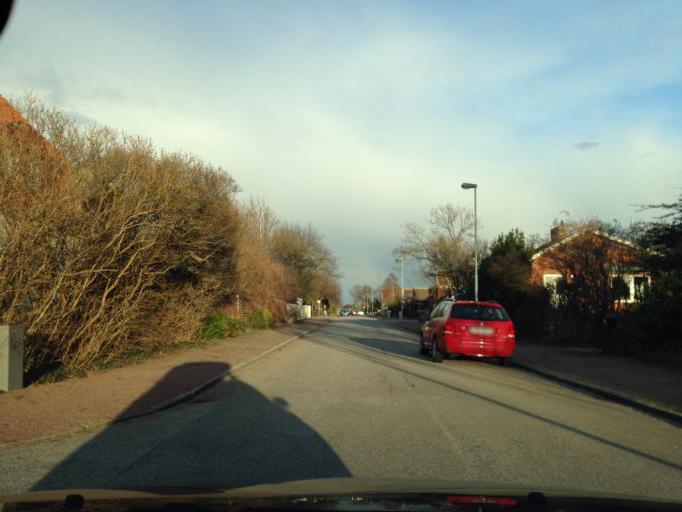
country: SE
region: Skane
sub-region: Malmo
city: Bunkeflostrand
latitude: 55.5817
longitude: 12.9484
